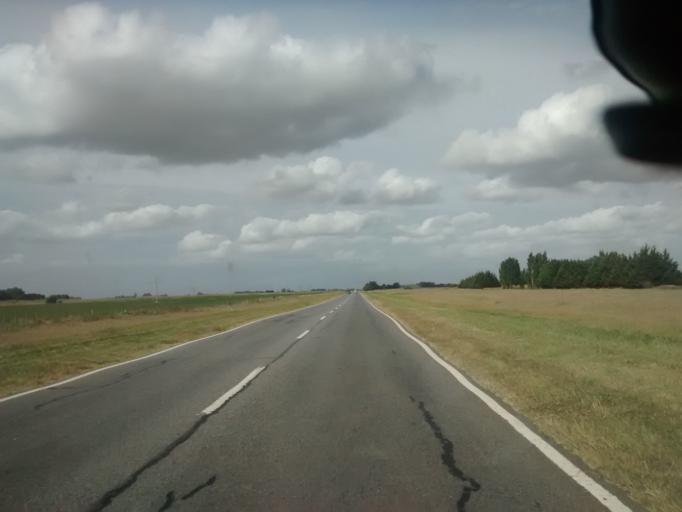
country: AR
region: Buenos Aires
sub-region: Partido de Balcarce
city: Balcarce
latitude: -37.6699
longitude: -58.5186
